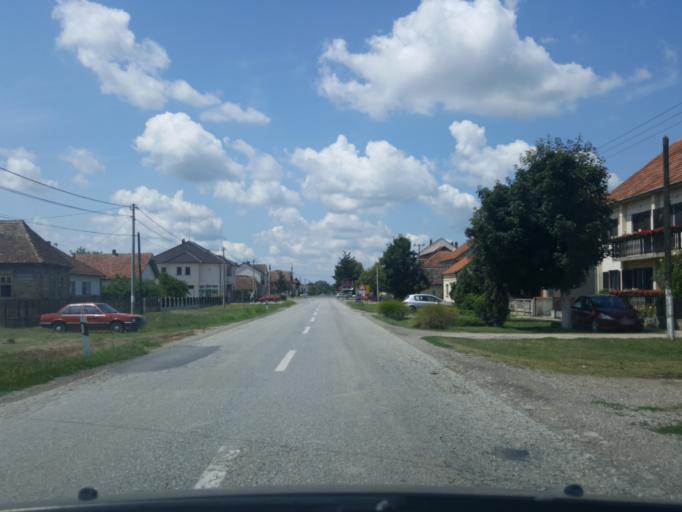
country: RS
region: Central Serbia
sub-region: Macvanski Okrug
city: Bogatic
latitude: 44.8413
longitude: 19.4838
